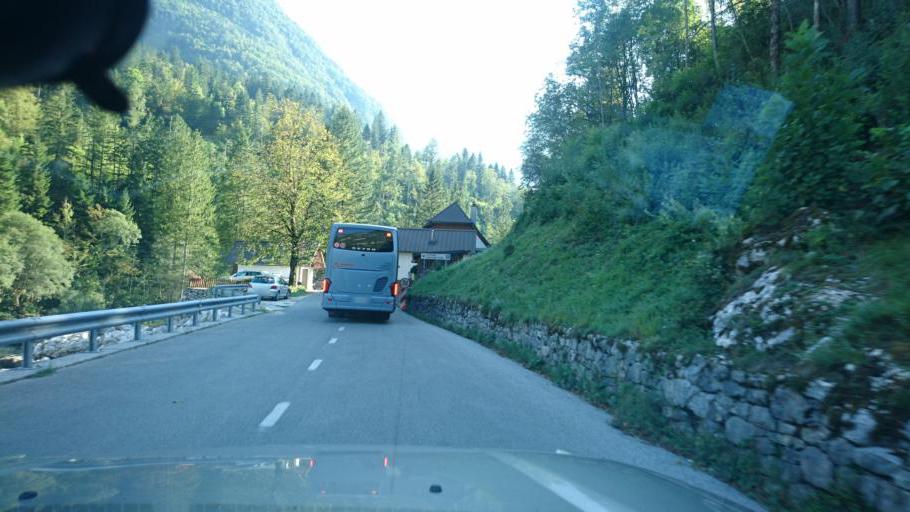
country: SI
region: Bovec
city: Bovec
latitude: 46.3412
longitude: 13.6593
